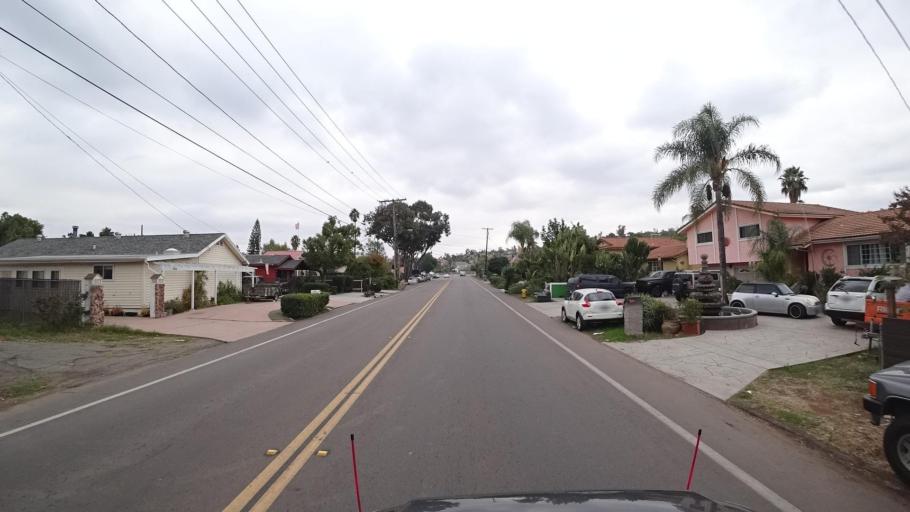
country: US
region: California
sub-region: San Diego County
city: Spring Valley
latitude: 32.7445
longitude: -116.9979
